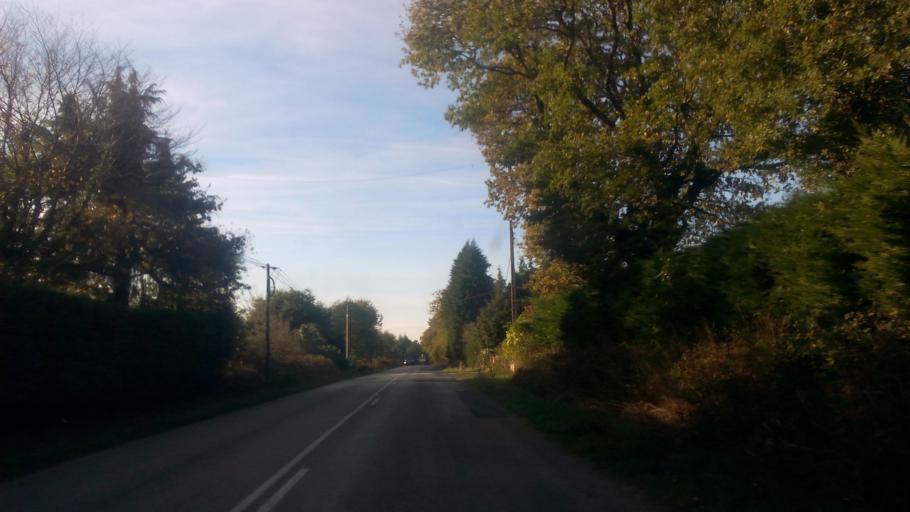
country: FR
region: Brittany
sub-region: Departement du Morbihan
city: La Vraie-Croix
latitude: 47.7083
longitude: -2.5582
